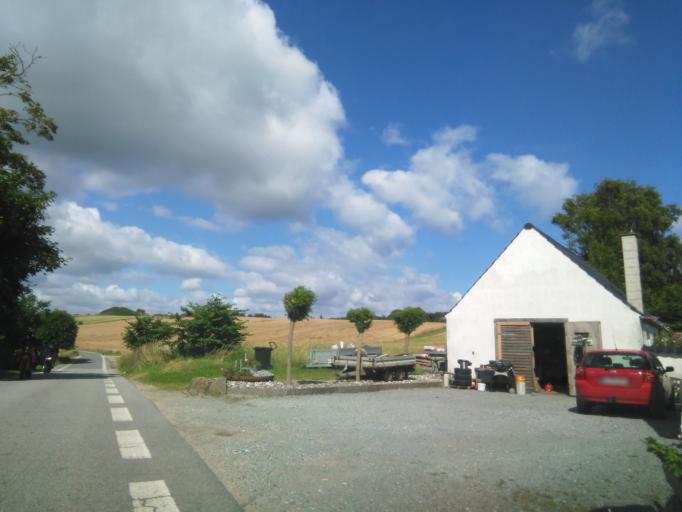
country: DK
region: Central Jutland
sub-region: Syddjurs Kommune
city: Ronde
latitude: 56.1812
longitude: 10.5114
